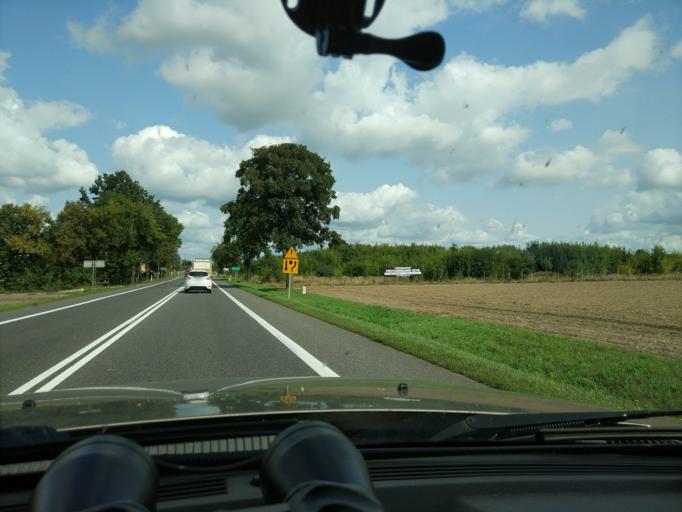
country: PL
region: Masovian Voivodeship
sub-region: Powiat mlawski
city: Wisniewo
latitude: 53.0571
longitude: 20.3459
